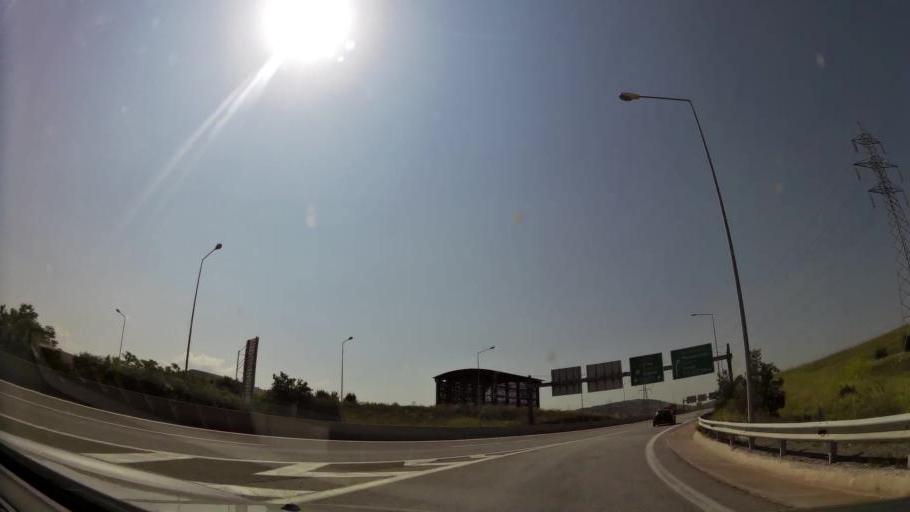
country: GR
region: West Macedonia
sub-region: Nomos Kozanis
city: Koila
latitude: 40.3501
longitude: 21.8041
